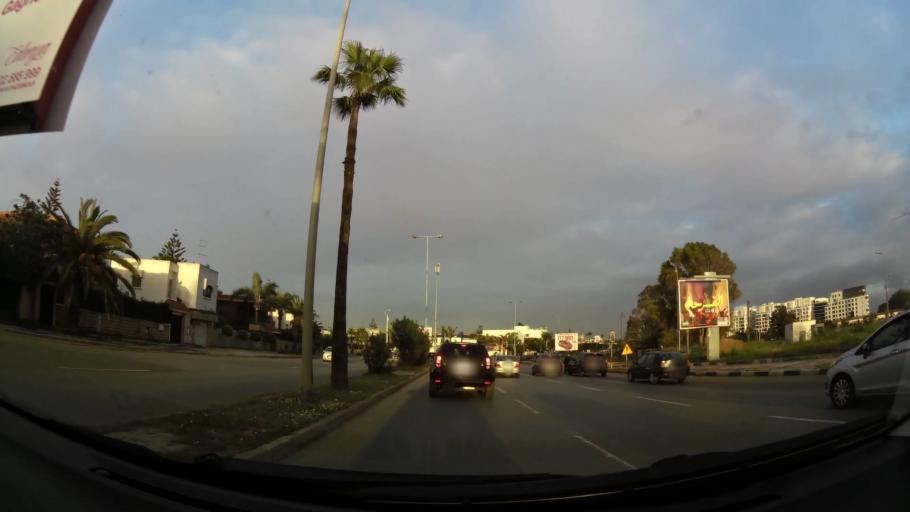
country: MA
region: Grand Casablanca
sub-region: Casablanca
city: Casablanca
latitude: 33.5699
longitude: -7.6632
